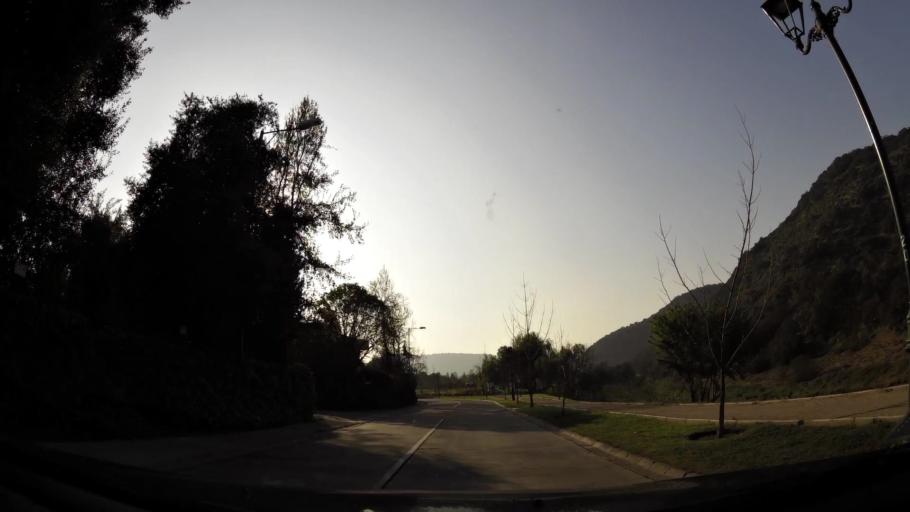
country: CL
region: Santiago Metropolitan
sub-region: Provincia de Santiago
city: Villa Presidente Frei, Nunoa, Santiago, Chile
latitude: -33.3481
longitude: -70.5377
